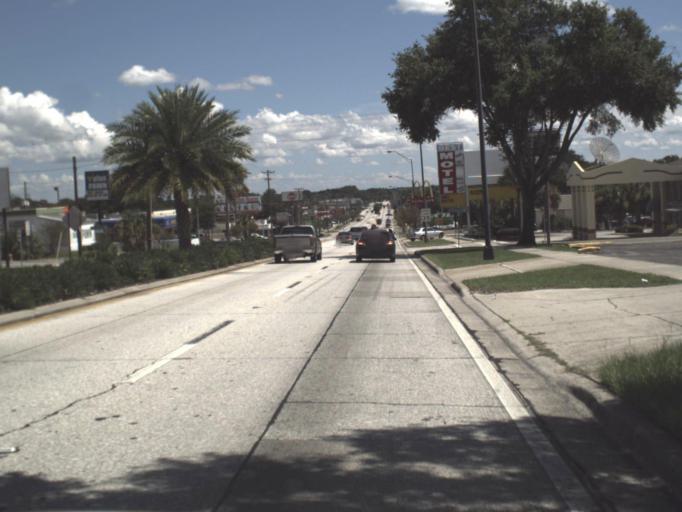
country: US
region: Florida
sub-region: Polk County
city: Lakeland
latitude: 28.0549
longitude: -81.9530
